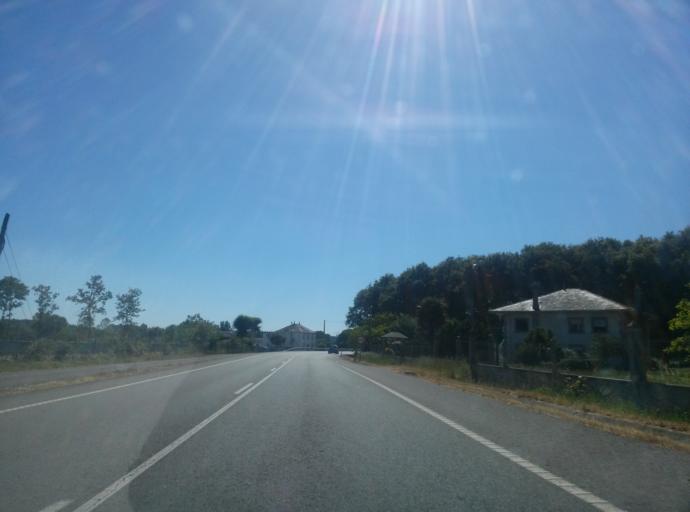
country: ES
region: Galicia
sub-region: Provincia de Lugo
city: Rabade
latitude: 43.1183
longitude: -7.5736
